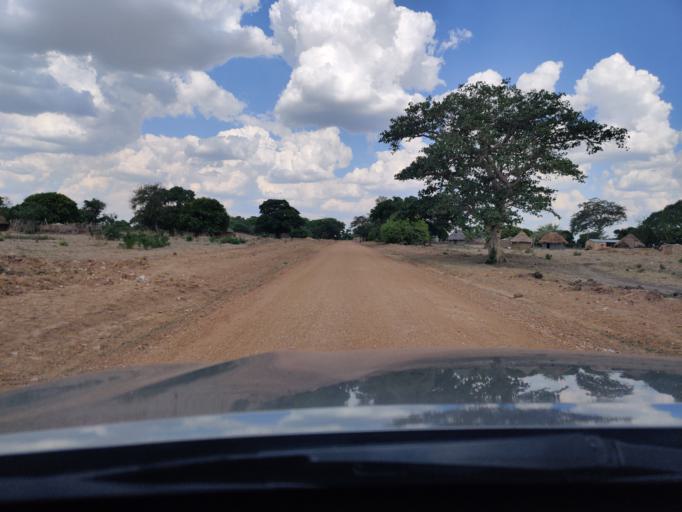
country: ZM
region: Central
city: Chibombo
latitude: -14.7615
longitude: 27.8938
